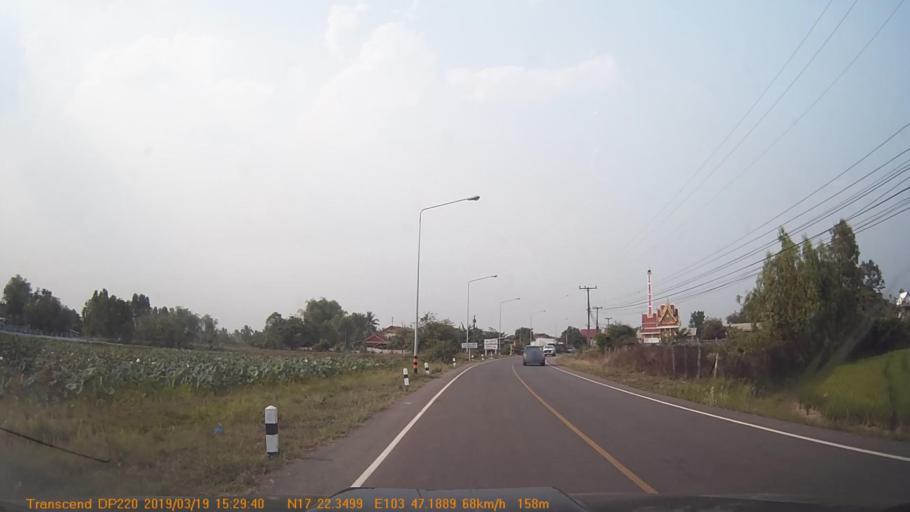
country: TH
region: Sakon Nakhon
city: Phanna Nikhom
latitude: 17.3728
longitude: 103.7864
